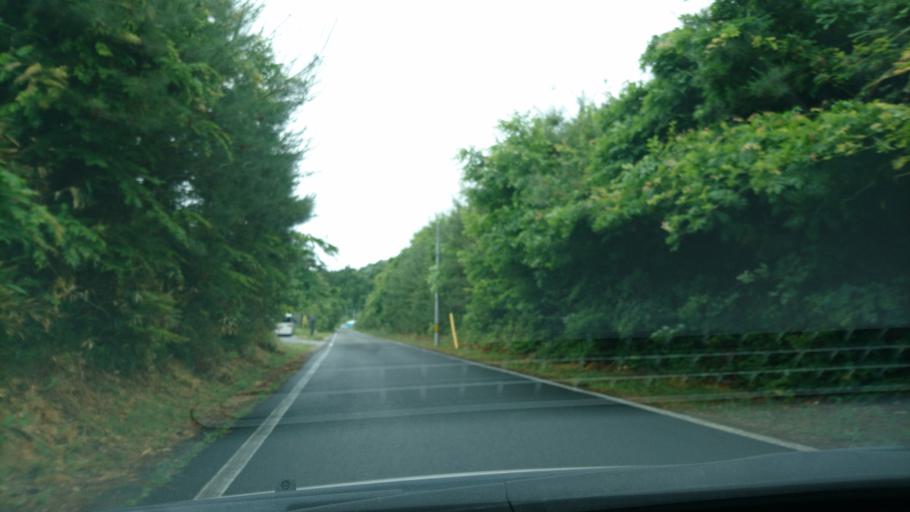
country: JP
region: Iwate
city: Ichinoseki
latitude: 38.8999
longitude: 141.1440
